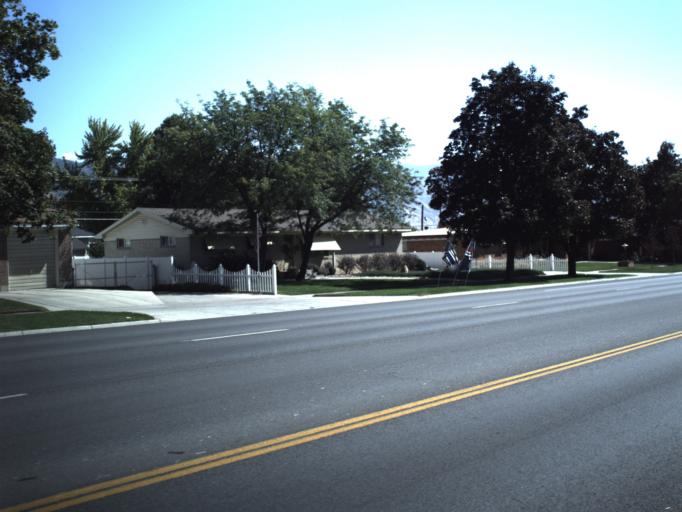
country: US
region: Utah
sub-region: Cache County
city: Smithfield
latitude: 41.8278
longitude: -111.8330
